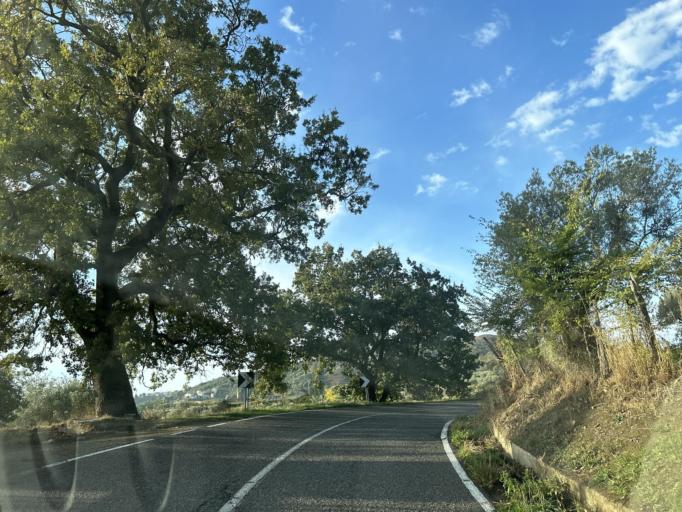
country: IT
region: Calabria
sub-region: Provincia di Catanzaro
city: Montauro
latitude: 38.7618
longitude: 16.5164
